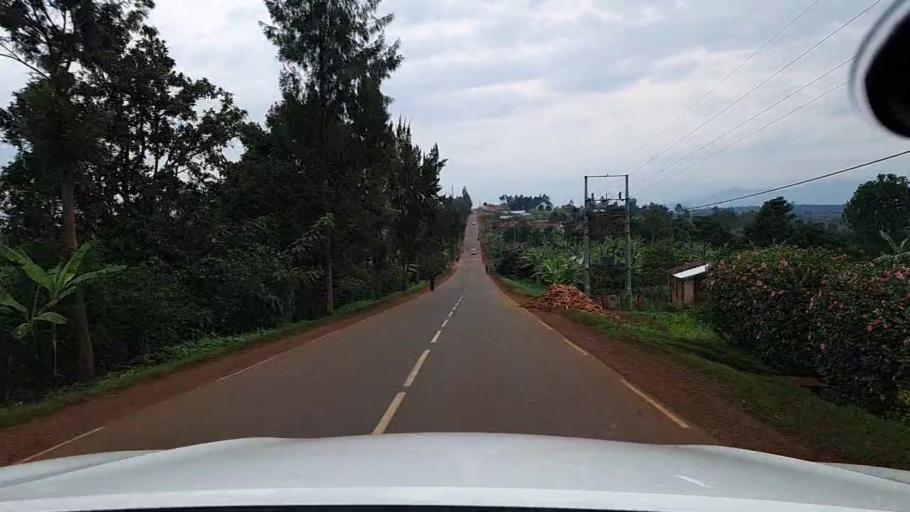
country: RW
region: Western Province
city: Cyangugu
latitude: -2.6306
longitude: 28.9517
